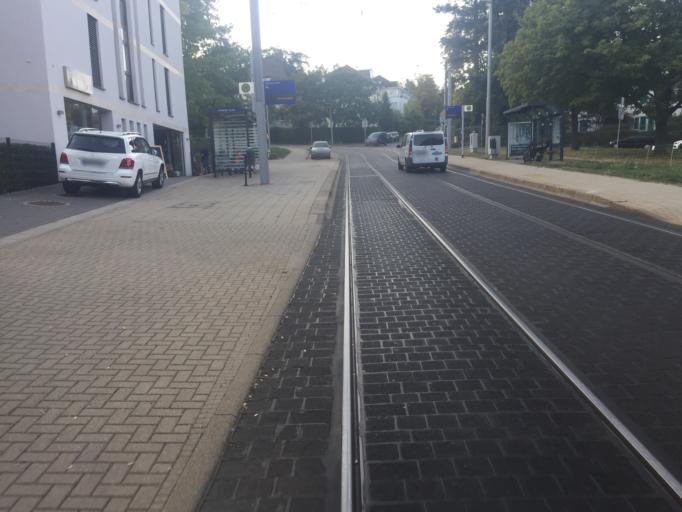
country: DE
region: Hesse
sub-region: Regierungsbezirk Kassel
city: Baunatal
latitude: 51.3094
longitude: 9.4226
